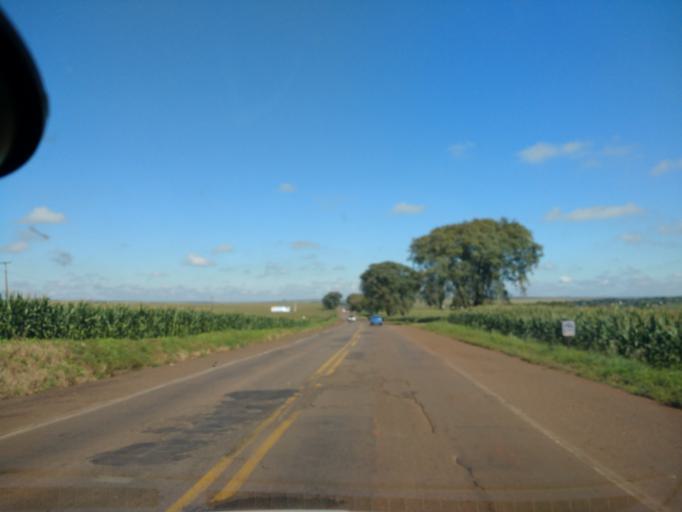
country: BR
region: Parana
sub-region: Terra Boa
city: Terra Boa
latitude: -23.6057
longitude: -52.4144
